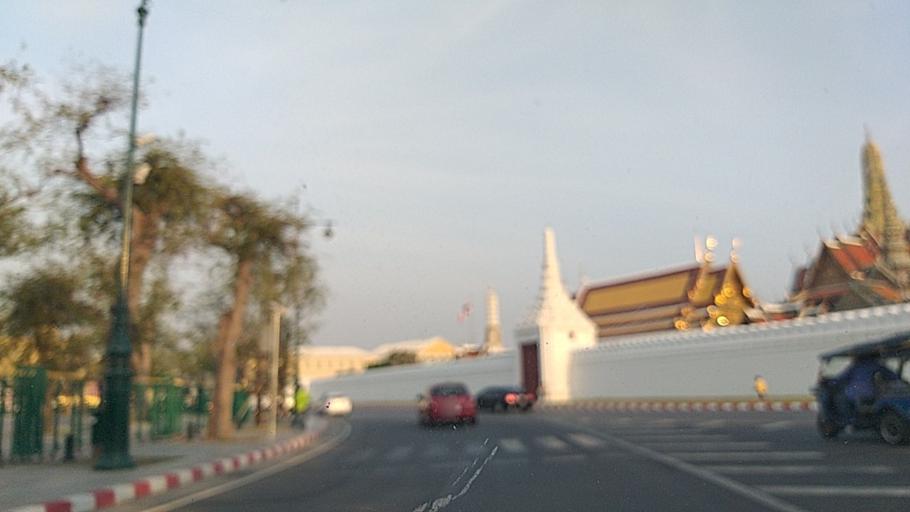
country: TH
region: Bangkok
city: Bangkok
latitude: 13.7526
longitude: 100.4920
